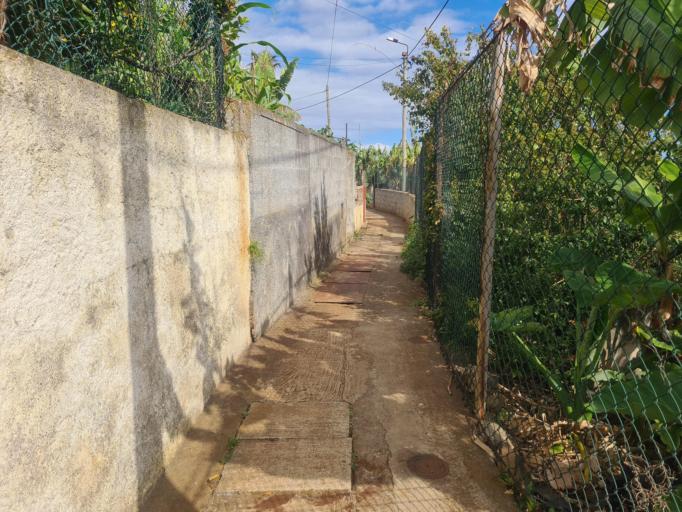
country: PT
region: Madeira
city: Camara de Lobos
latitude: 32.6549
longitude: -16.9453
